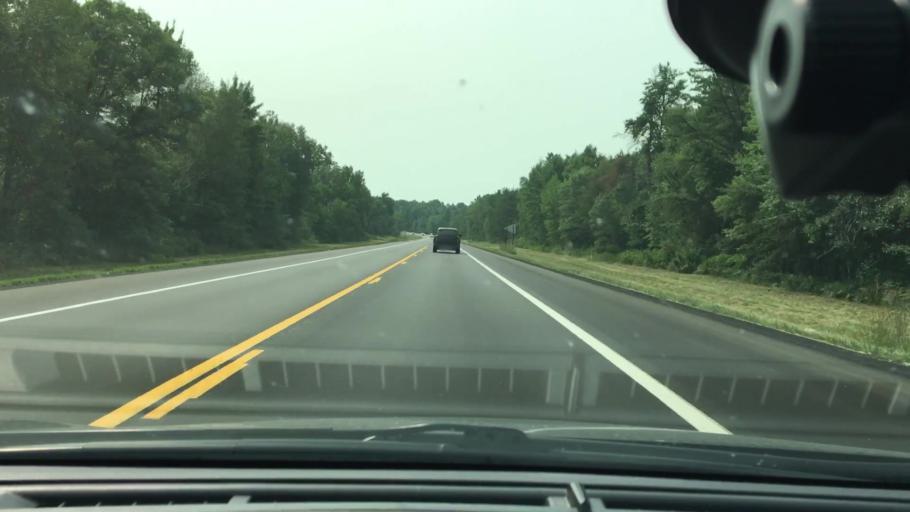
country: US
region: Minnesota
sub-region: Crow Wing County
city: Brainerd
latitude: 46.4225
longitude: -94.1787
